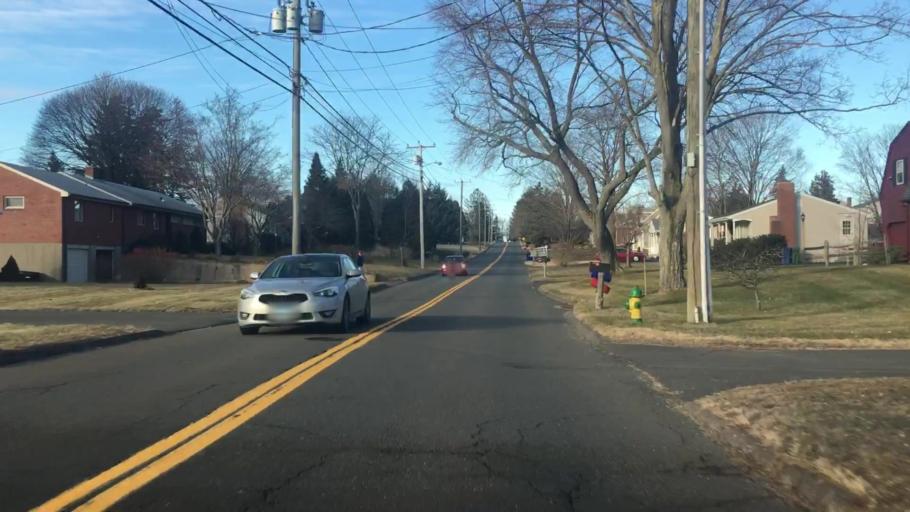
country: US
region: Connecticut
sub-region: Middlesex County
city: Middletown
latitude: 41.5278
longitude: -72.6502
